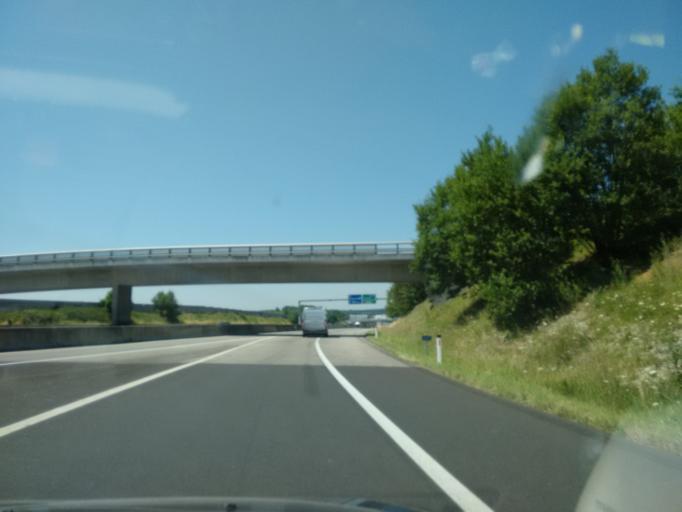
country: AT
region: Upper Austria
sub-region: Wels-Land
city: Sattledt
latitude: 48.0660
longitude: 14.0336
